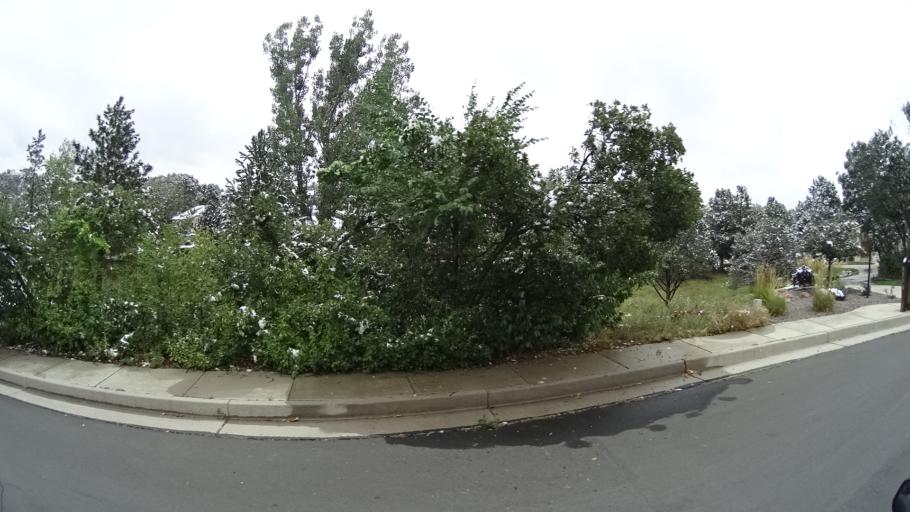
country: US
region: Colorado
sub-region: El Paso County
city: Colorado Springs
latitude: 38.9162
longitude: -104.8015
